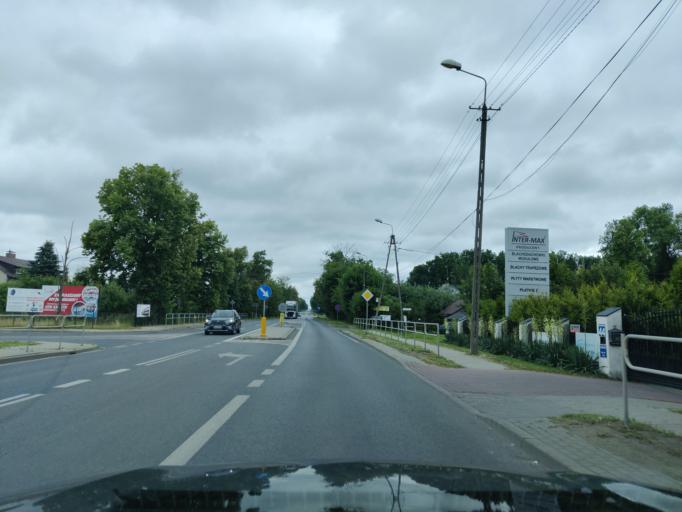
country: PL
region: Masovian Voivodeship
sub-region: Powiat pultuski
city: Pultusk
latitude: 52.6905
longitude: 21.0805
